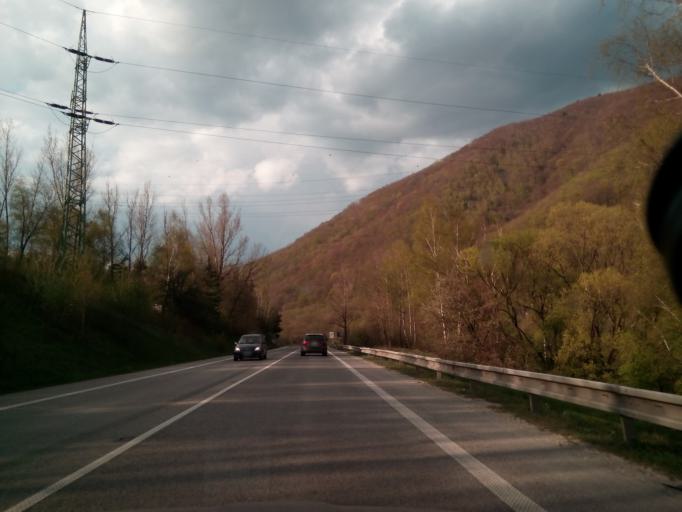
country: SK
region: Zilinsky
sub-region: Okres Zilina
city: Vrutky
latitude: 49.1380
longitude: 18.8913
